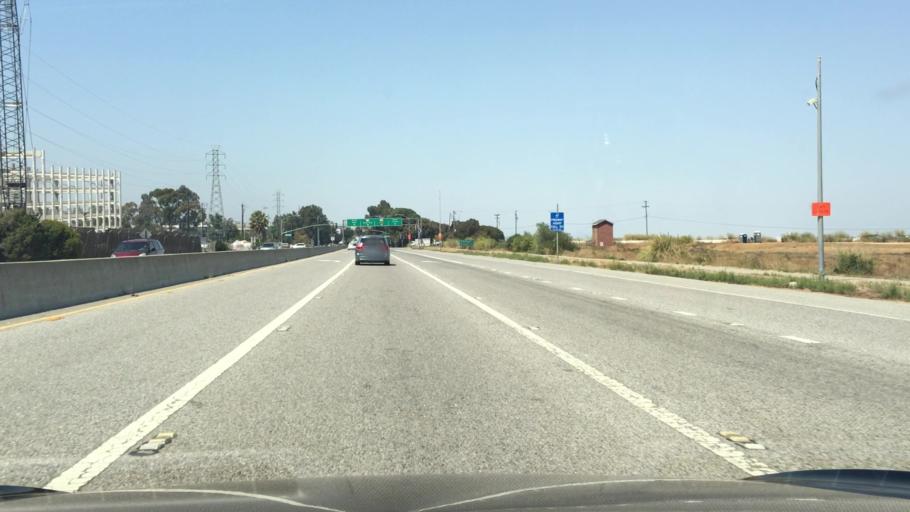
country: US
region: California
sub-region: San Mateo County
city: North Fair Oaks
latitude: 37.4857
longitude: -122.1756
